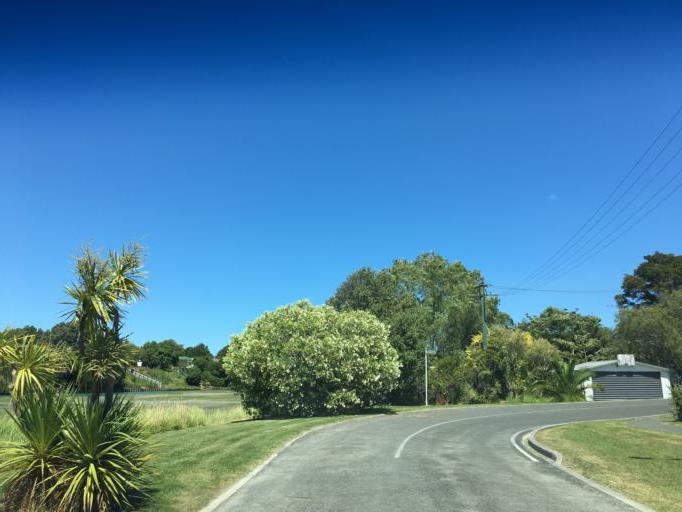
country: NZ
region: Gisborne
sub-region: Gisborne District
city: Gisborne
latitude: -38.6591
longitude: 178.0248
